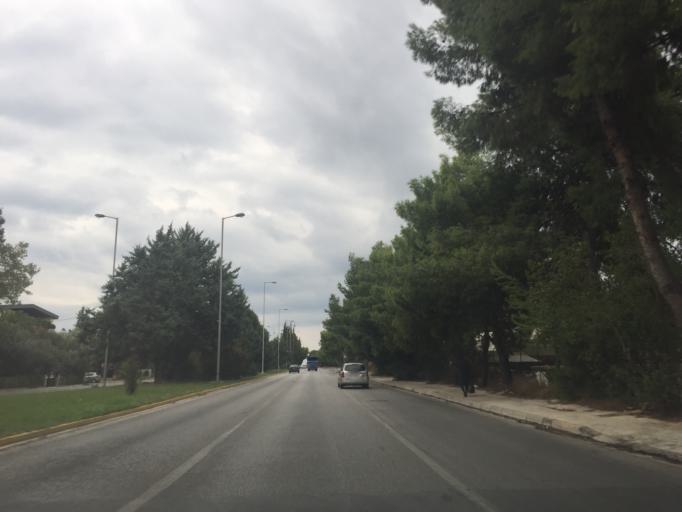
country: GR
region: Attica
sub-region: Nomarchia Anatolikis Attikis
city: Vouliagmeni
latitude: 37.8260
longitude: 23.7742
